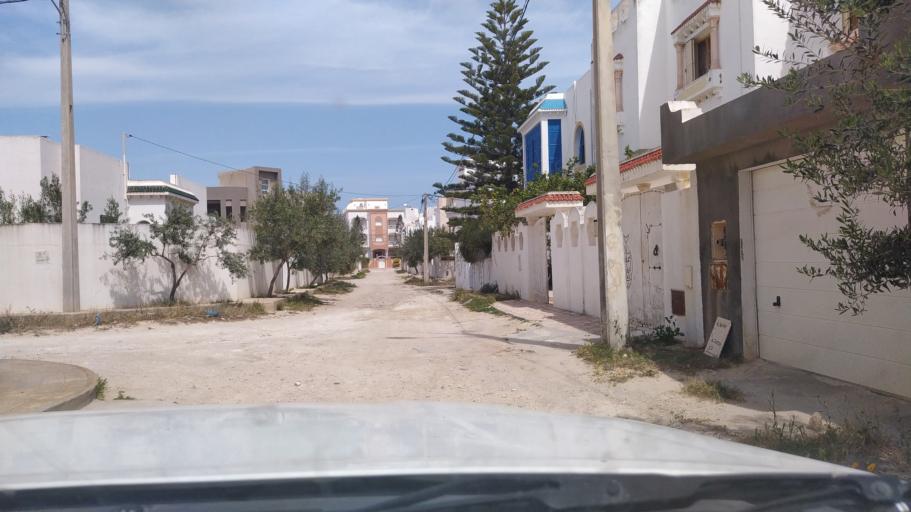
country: TN
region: Al Mahdiyah
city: Mahdia
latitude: 35.5202
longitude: 11.0402
